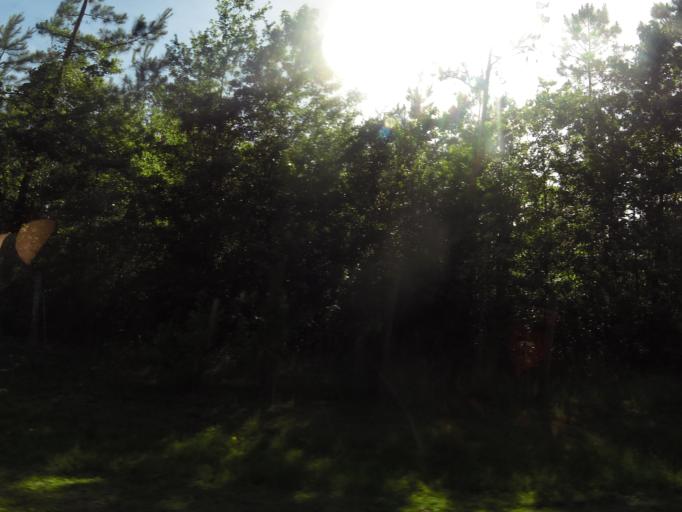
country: US
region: Florida
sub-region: Nassau County
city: Callahan
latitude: 30.5533
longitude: -81.7927
